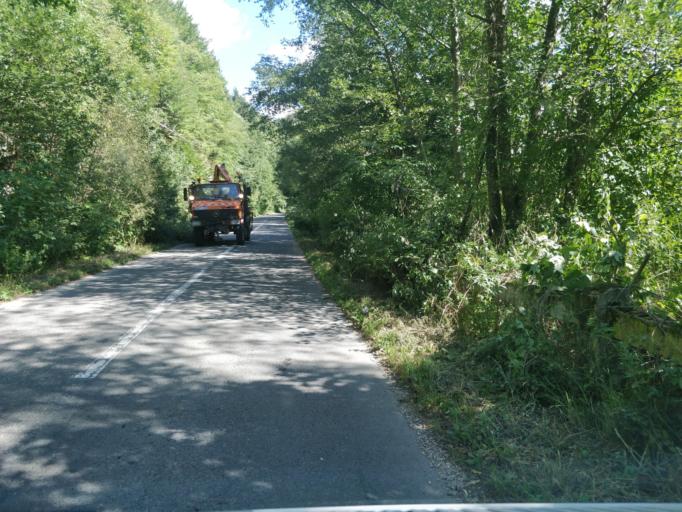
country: RO
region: Cluj
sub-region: Comuna Sacueu
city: Sacuieu
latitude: 46.8518
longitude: 22.8615
